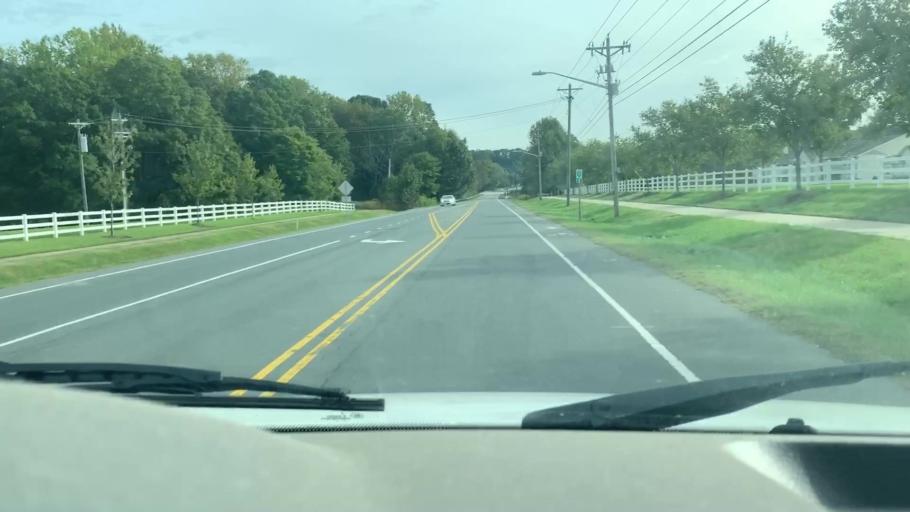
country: US
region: North Carolina
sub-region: Mecklenburg County
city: Cornelius
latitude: 35.4627
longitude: -80.8799
